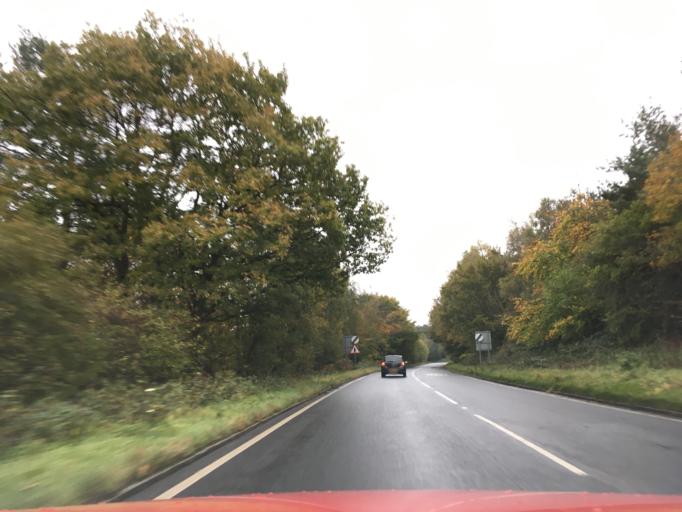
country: GB
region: England
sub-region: West Berkshire
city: Welford
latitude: 51.4245
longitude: -1.3961
